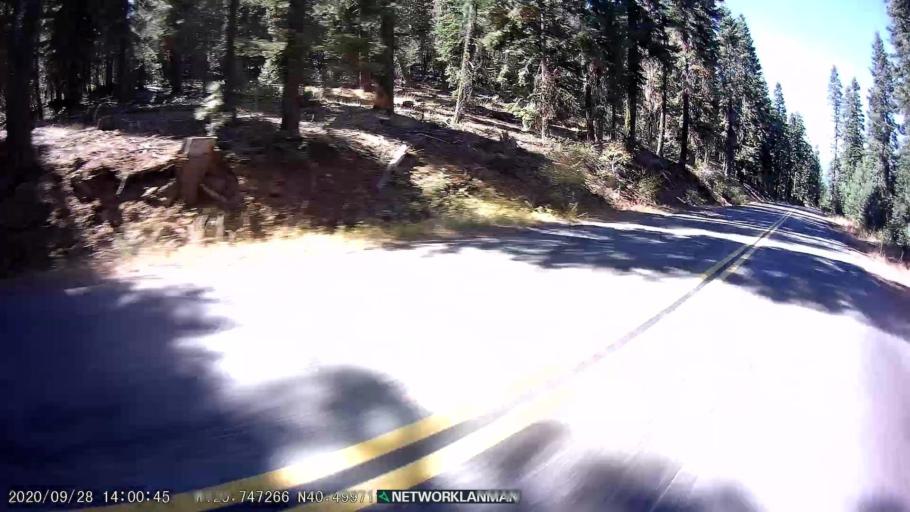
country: US
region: California
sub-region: Lassen County
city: Susanville
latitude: 40.5000
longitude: -120.7476
